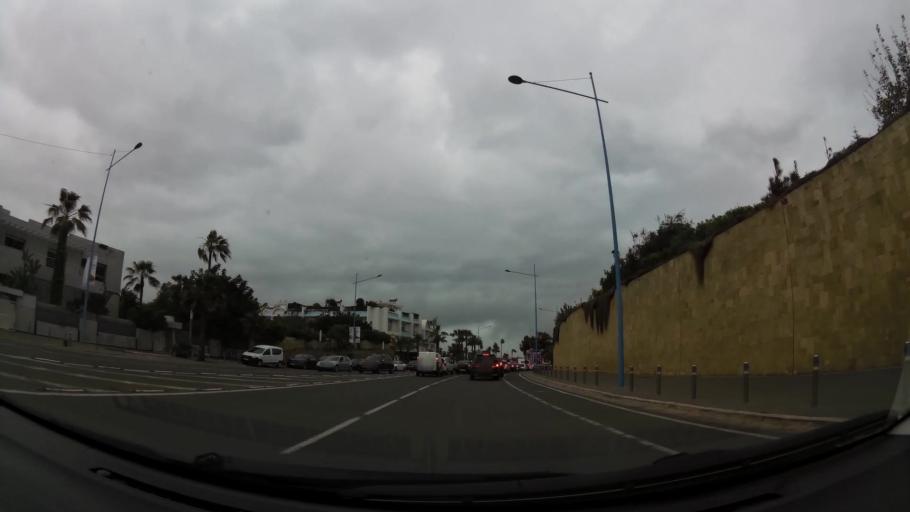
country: MA
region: Grand Casablanca
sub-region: Casablanca
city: Casablanca
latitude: 33.5942
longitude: -7.6672
